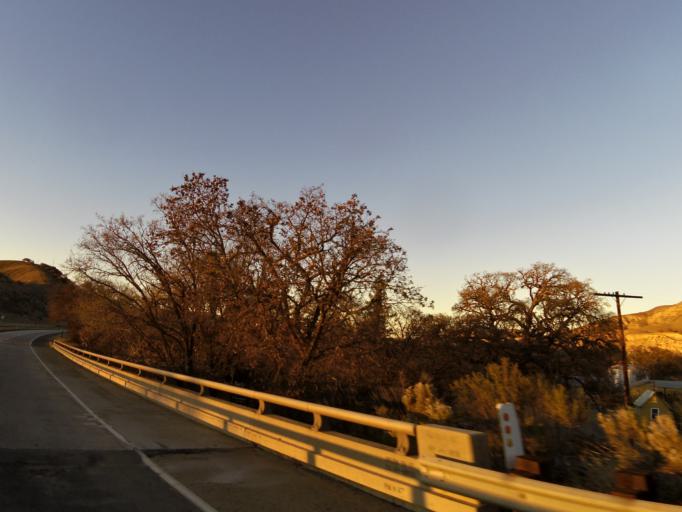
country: US
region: California
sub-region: San Luis Obispo County
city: Lake Nacimiento
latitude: 35.8737
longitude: -120.8353
